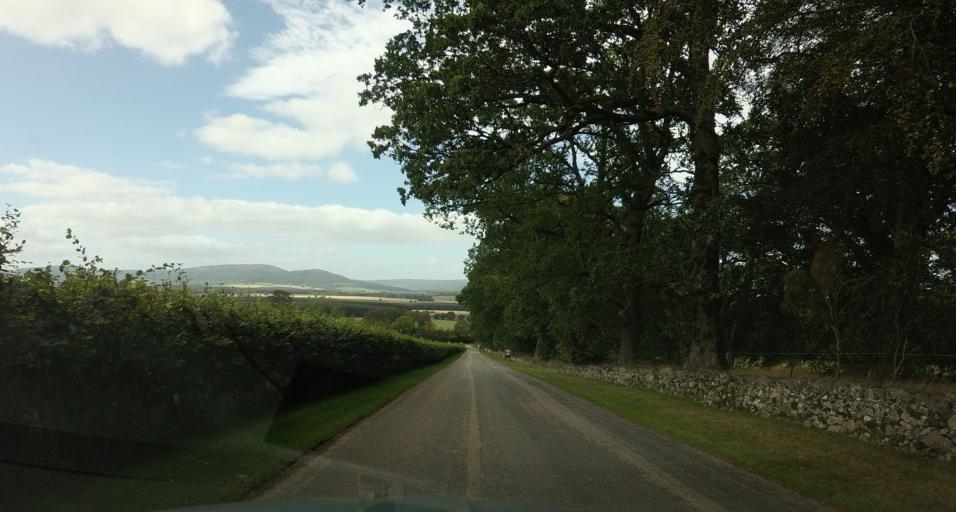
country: GB
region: Scotland
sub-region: Aberdeenshire
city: Kemnay
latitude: 57.2063
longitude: -2.4656
